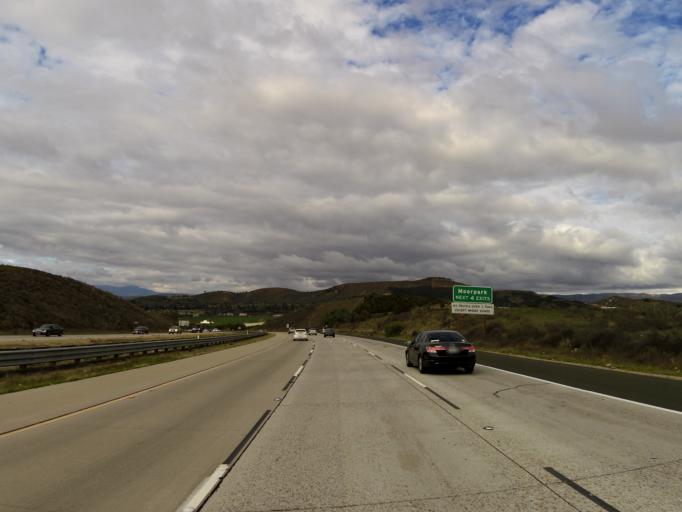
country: US
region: California
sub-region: Ventura County
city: Moorpark
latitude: 34.2545
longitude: -118.8402
